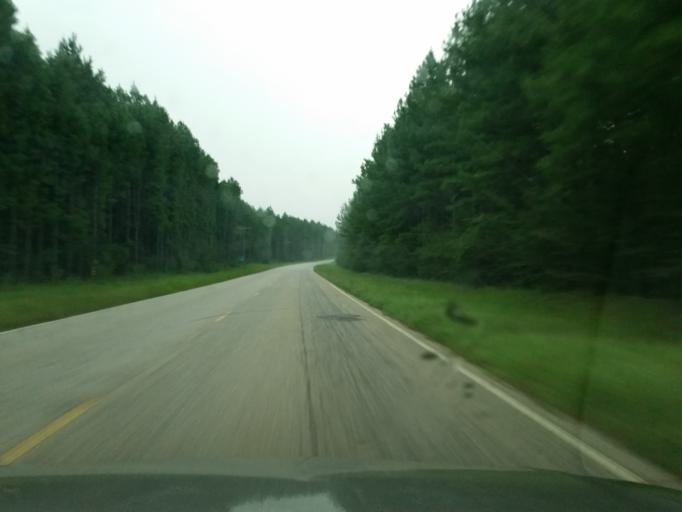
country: US
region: Florida
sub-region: Escambia County
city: Cantonment
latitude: 30.6927
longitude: -87.5092
